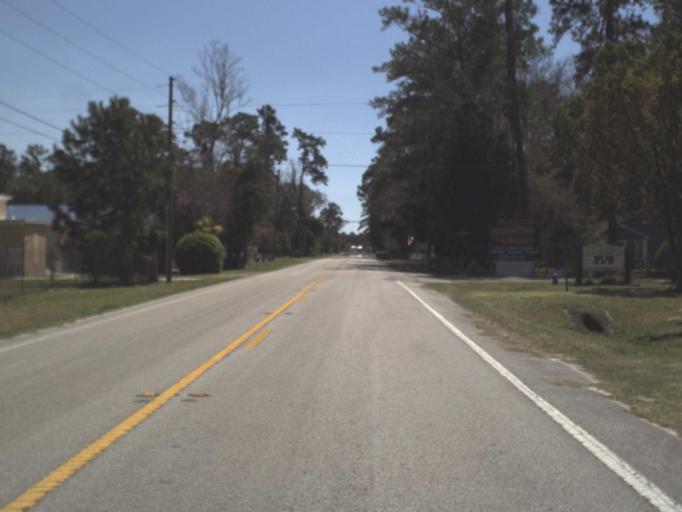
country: US
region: Florida
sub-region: Leon County
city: Woodville
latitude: 30.1616
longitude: -84.2063
